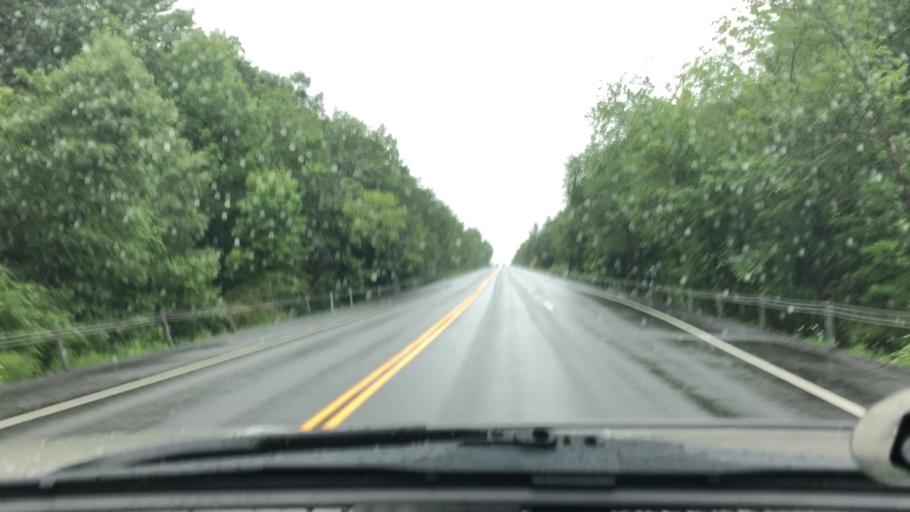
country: US
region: New York
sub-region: Greene County
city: Cairo
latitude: 42.3055
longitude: -74.0444
